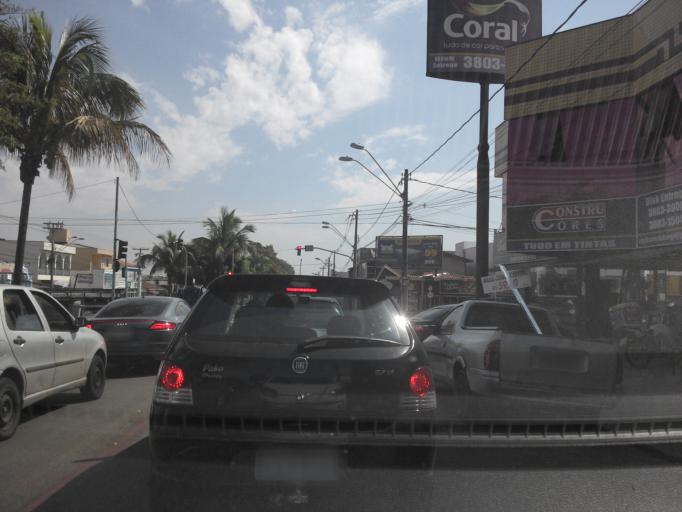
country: BR
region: Sao Paulo
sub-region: Sumare
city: Sumare
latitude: -22.8192
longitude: -47.2744
